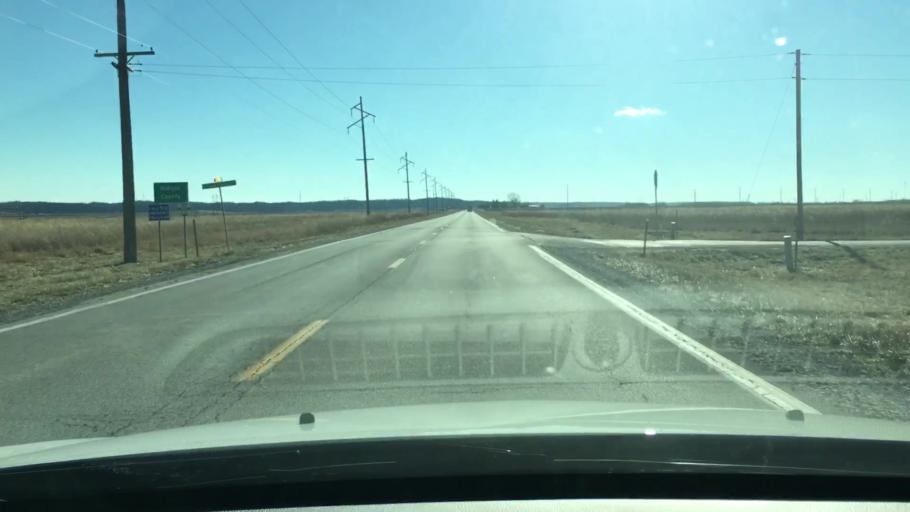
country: US
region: Illinois
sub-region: Morgan County
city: Meredosia
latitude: 39.8765
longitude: -90.5053
